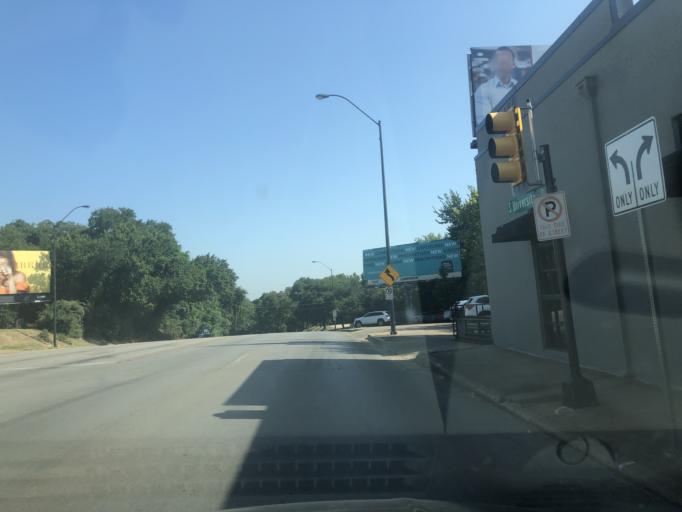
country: US
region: Texas
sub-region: Tarrant County
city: Fort Worth
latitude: 32.7162
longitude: -97.3603
